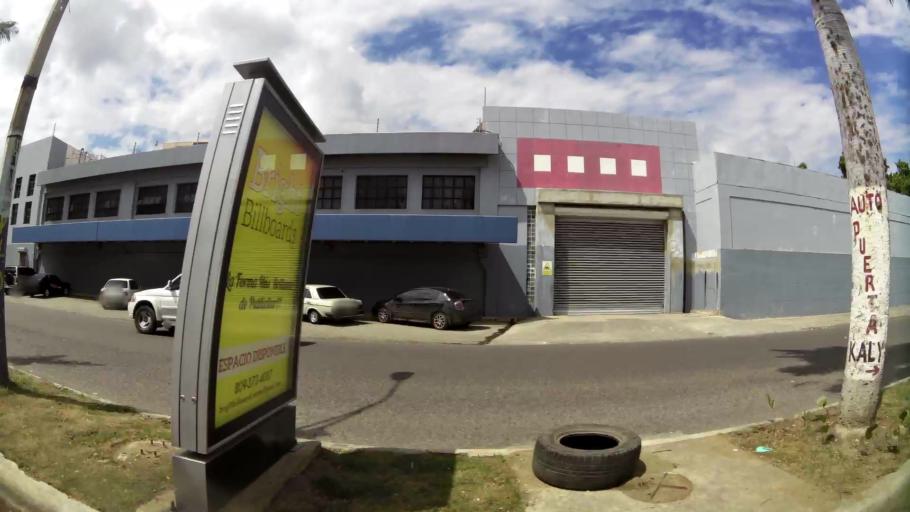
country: DO
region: Santiago
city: Santiago de los Caballeros
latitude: 19.4598
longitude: -70.7095
